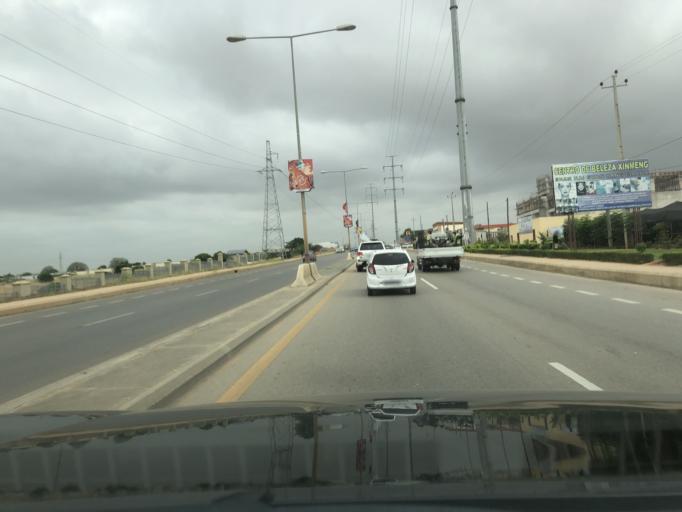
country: AO
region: Luanda
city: Luanda
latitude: -8.9667
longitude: 13.2062
